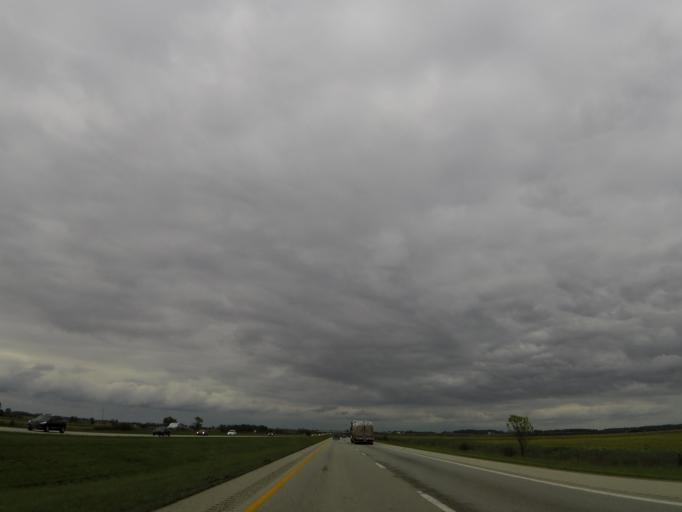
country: US
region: Ohio
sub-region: Greene County
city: Shawnee Hills
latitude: 39.5427
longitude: -83.7622
